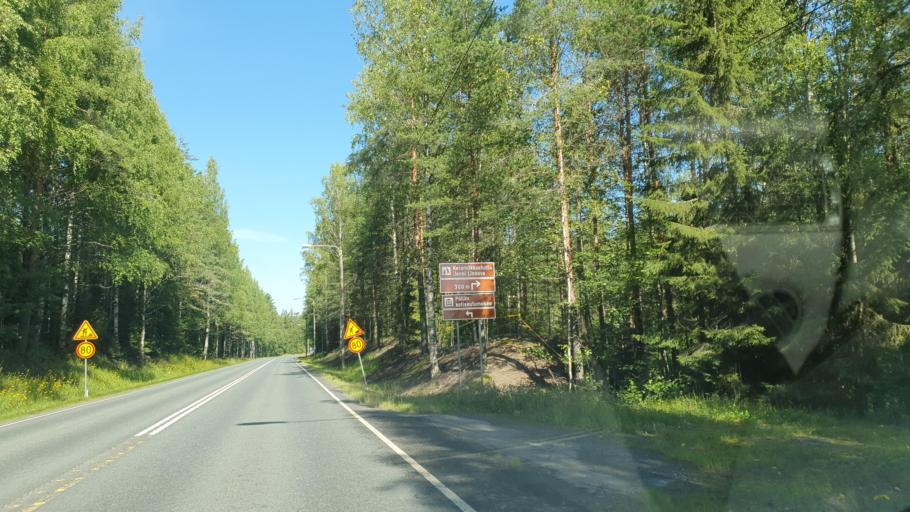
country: FI
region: Northern Savo
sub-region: Kuopio
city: Siilinjaervi
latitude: 63.1227
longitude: 27.6299
